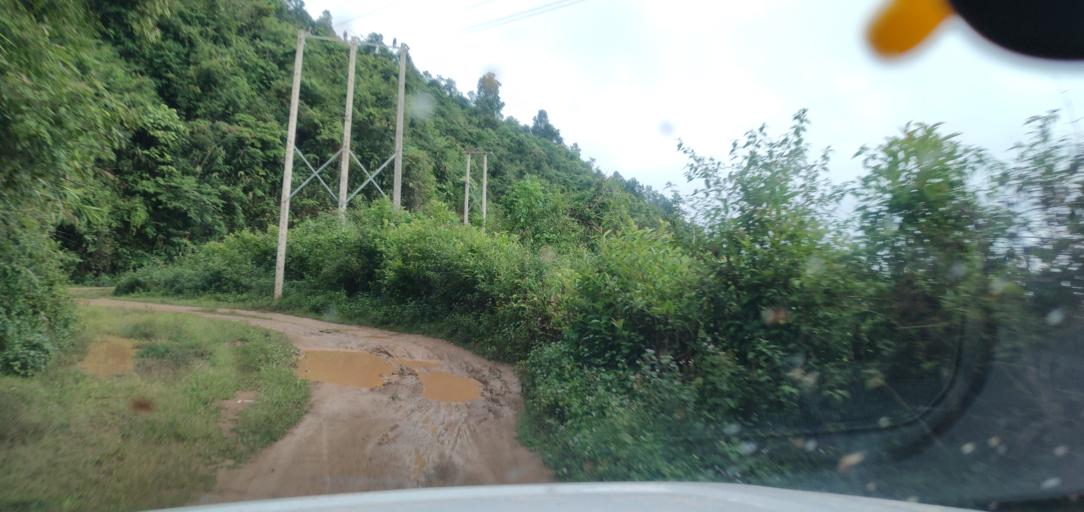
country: LA
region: Phongsali
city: Phongsali
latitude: 21.4465
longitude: 102.2926
